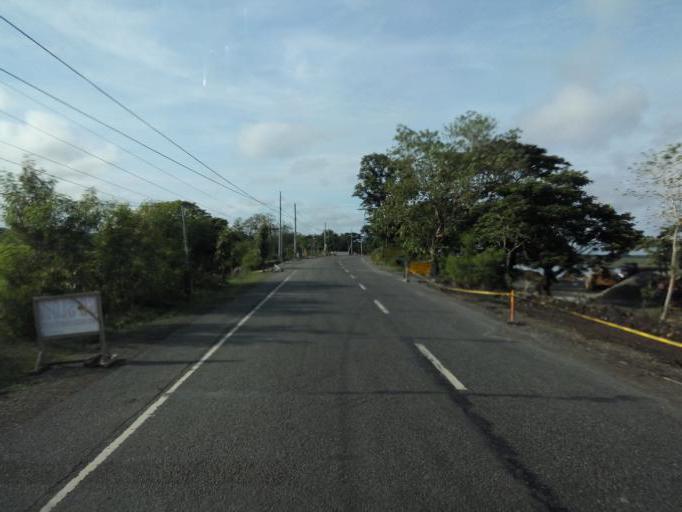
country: PH
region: Cagayan Valley
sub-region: Province of Cagayan
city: Divisoria
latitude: 17.5372
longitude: 121.7879
